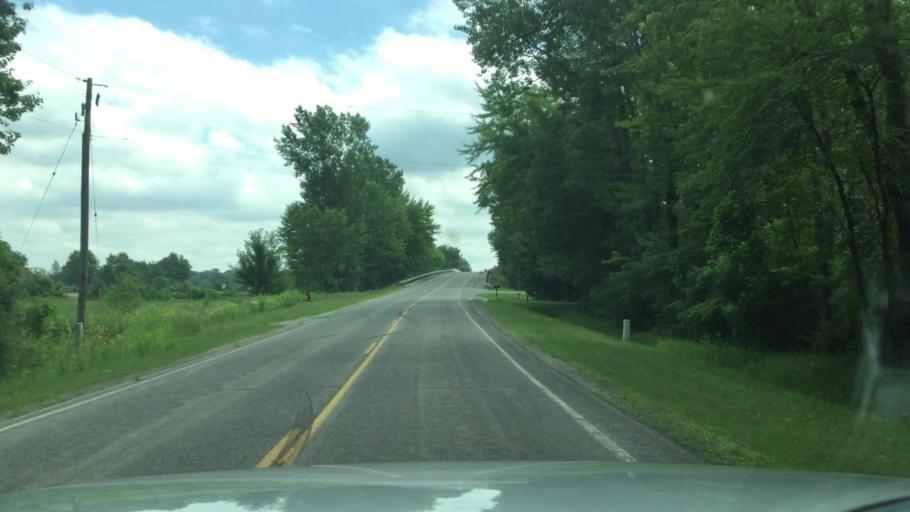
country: US
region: Michigan
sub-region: Saginaw County
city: Birch Run
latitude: 43.2942
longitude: -83.8241
